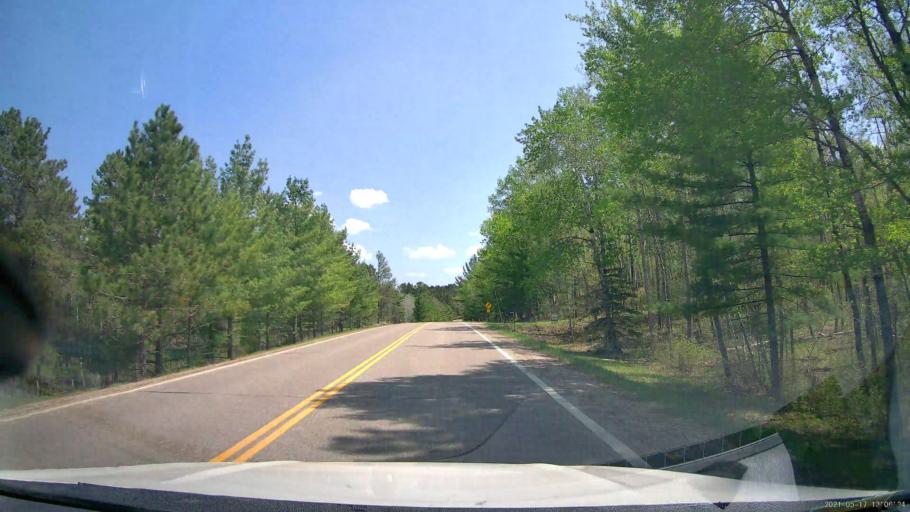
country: US
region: Minnesota
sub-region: Hubbard County
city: Park Rapids
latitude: 47.0541
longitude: -94.9271
